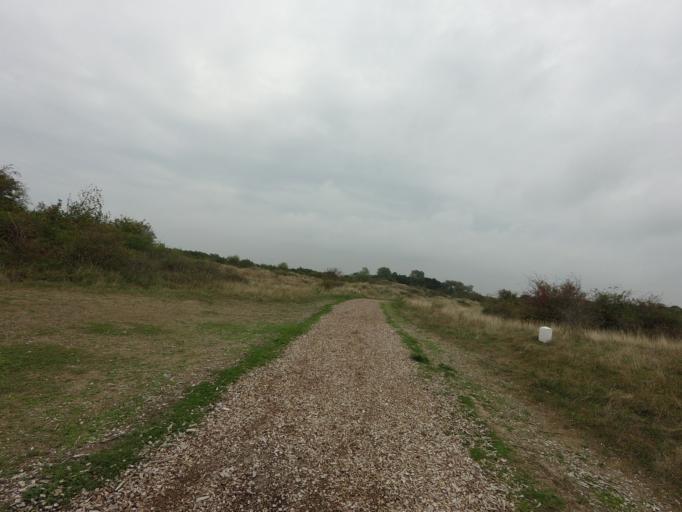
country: NL
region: Friesland
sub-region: Gemeente Schiermonnikoog
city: Schiermonnikoog
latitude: 53.4865
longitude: 6.1822
